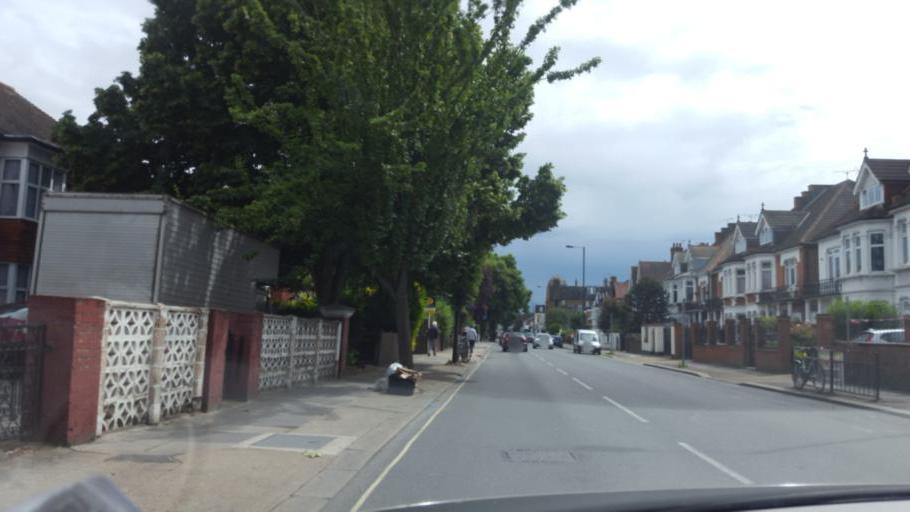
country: GB
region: England
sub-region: Greater London
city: Hammersmith
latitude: 51.5085
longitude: -0.2456
